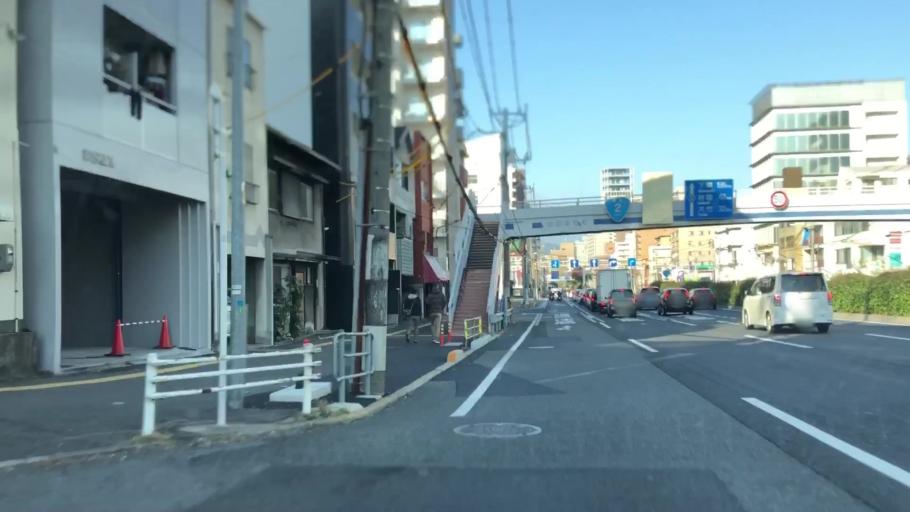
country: JP
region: Hiroshima
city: Hiroshima-shi
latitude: 34.3818
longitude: 132.4638
